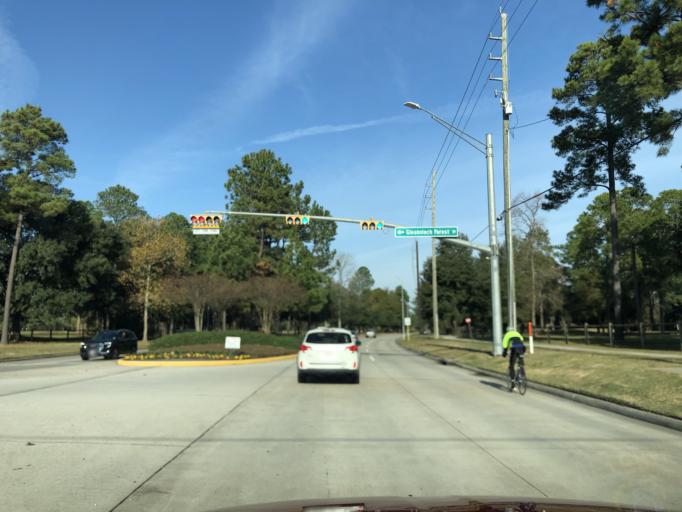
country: US
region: Texas
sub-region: Harris County
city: Tomball
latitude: 30.0369
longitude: -95.5612
